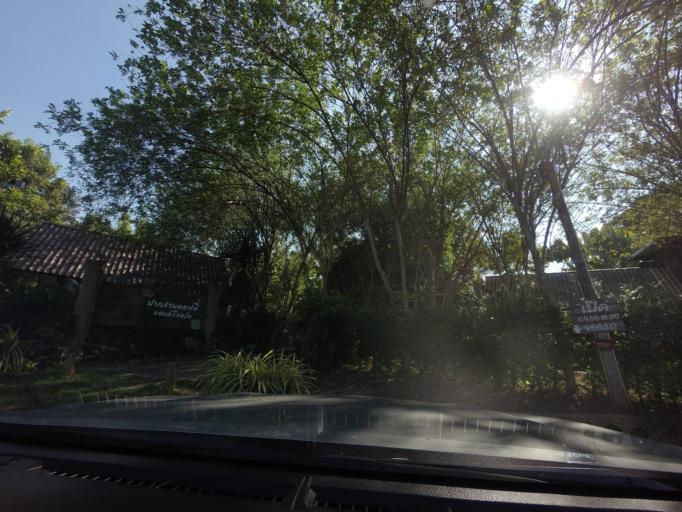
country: TH
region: Sukhothai
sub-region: Amphoe Si Satchanalai
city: Si Satchanalai
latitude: 17.6300
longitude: 99.6867
